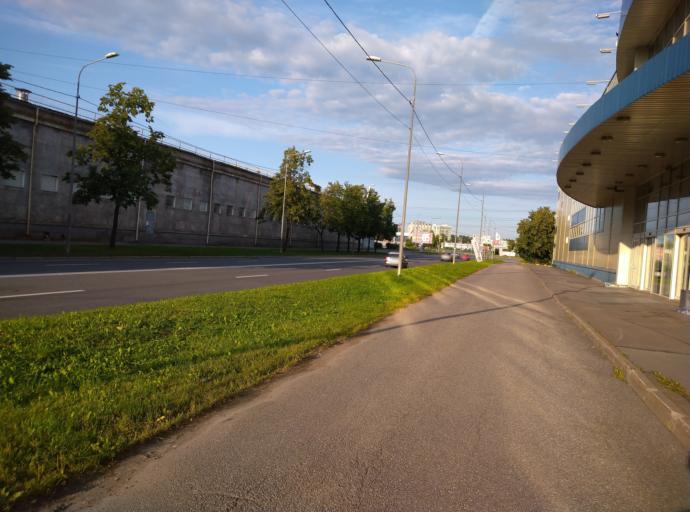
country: RU
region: St.-Petersburg
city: Kupchino
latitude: 59.8719
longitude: 30.3408
